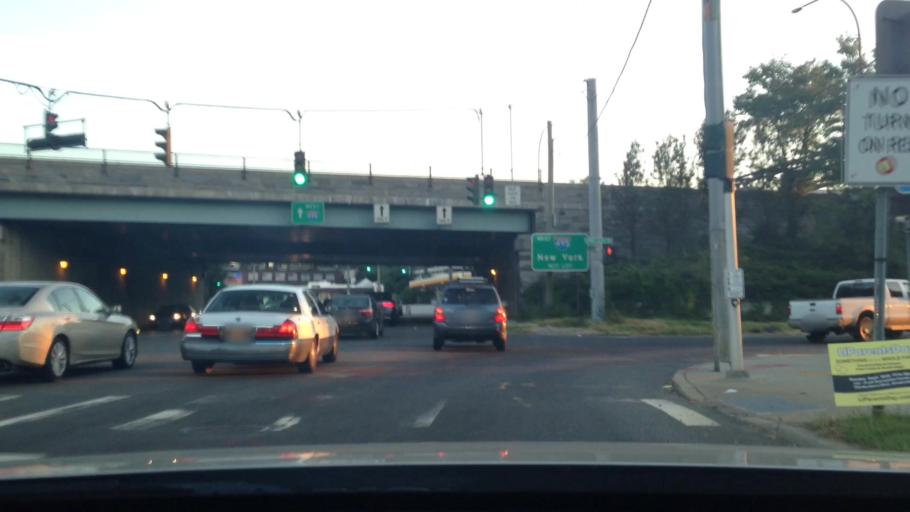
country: US
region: New York
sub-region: Nassau County
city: Roslyn Heights
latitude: 40.7843
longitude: -73.6489
